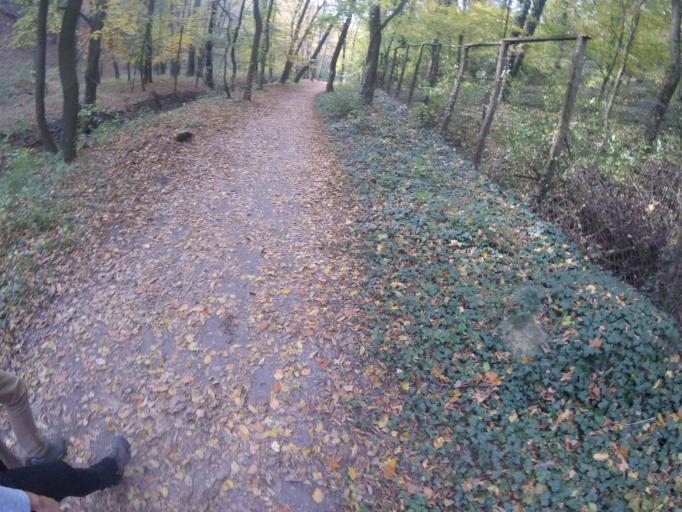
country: HU
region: Fejer
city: Bodajk
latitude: 47.3142
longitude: 18.2148
